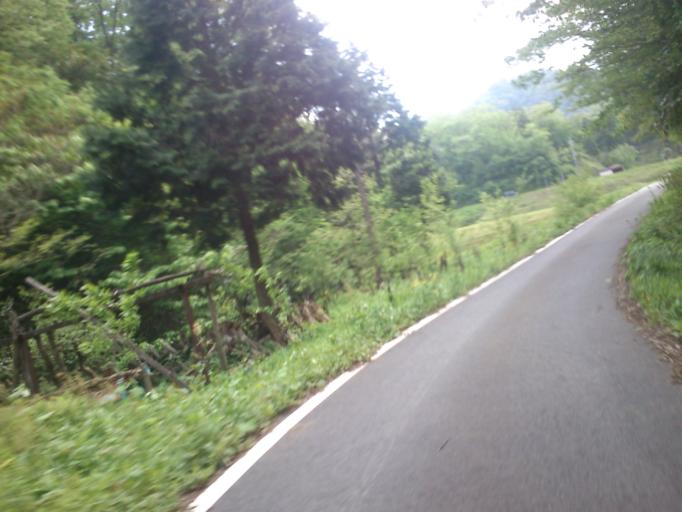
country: JP
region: Kyoto
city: Miyazu
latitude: 35.6942
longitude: 135.1353
